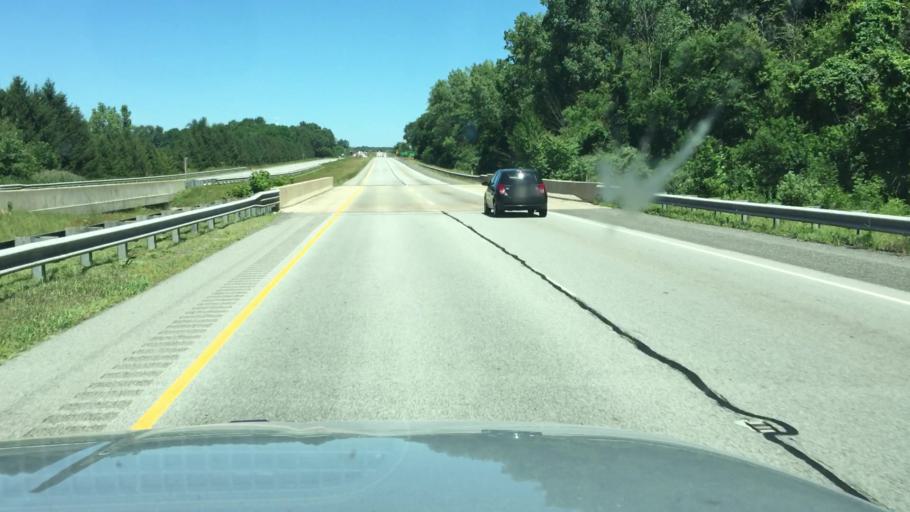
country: US
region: Indiana
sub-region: Porter County
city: Chesterton
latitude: 41.5984
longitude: -87.0443
